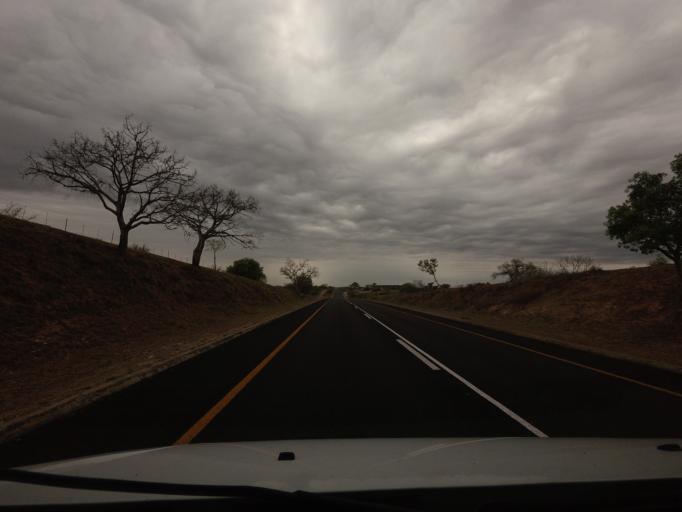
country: ZA
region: Limpopo
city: Thulamahashi
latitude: -24.5683
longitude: 31.0789
